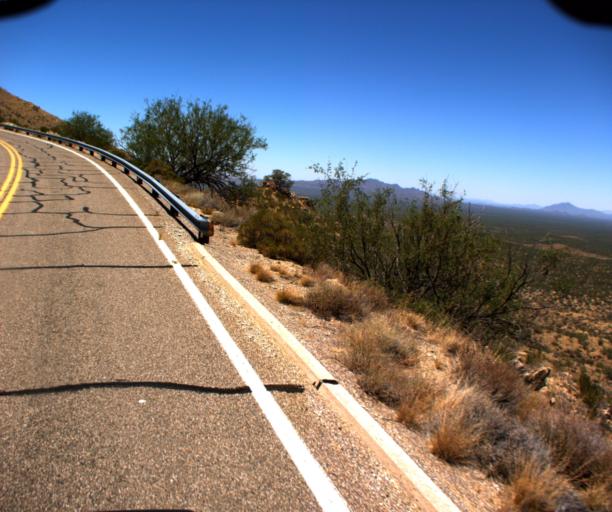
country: US
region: Arizona
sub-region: Pima County
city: Three Points
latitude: 31.9887
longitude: -111.5917
